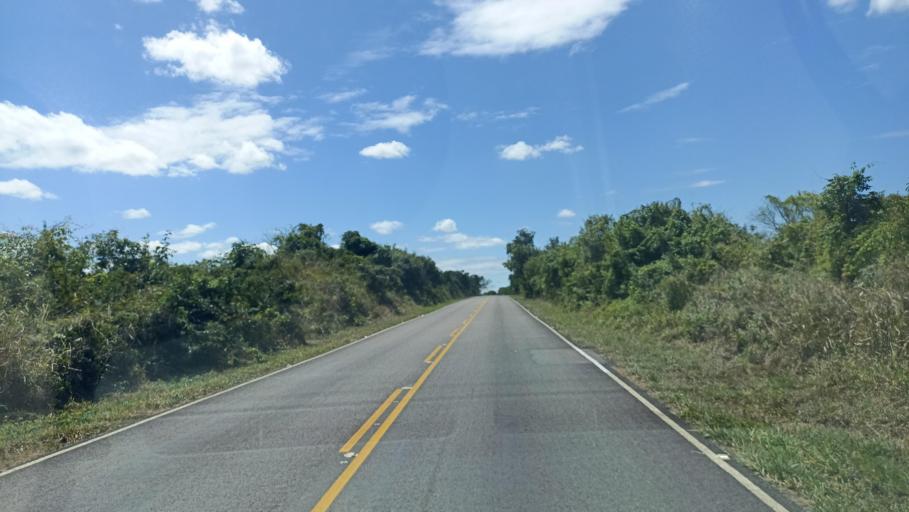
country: BR
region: Bahia
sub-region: Andarai
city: Vera Cruz
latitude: -12.7489
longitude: -41.3256
